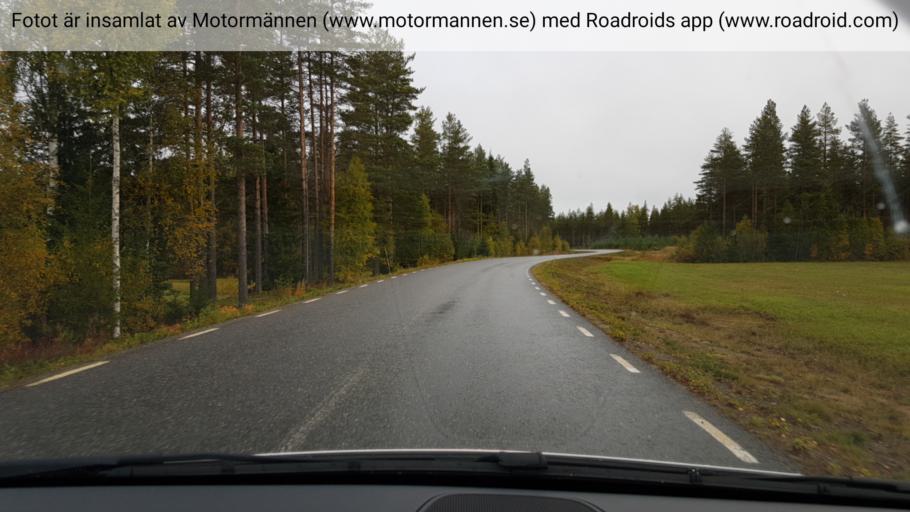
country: SE
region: Vaesterbotten
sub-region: Umea Kommun
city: Ersmark
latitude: 64.1302
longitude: 20.3871
